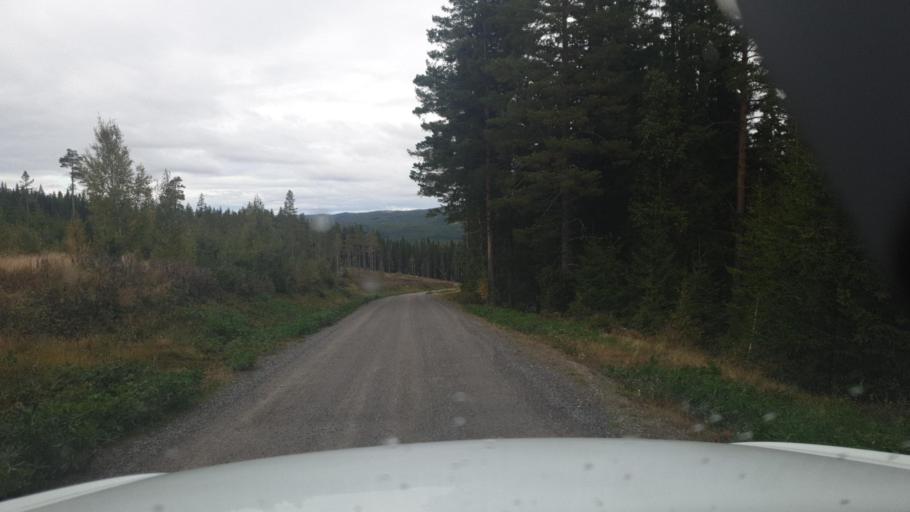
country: SE
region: Vaermland
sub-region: Torsby Kommun
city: Torsby
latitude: 60.1755
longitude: 12.6463
